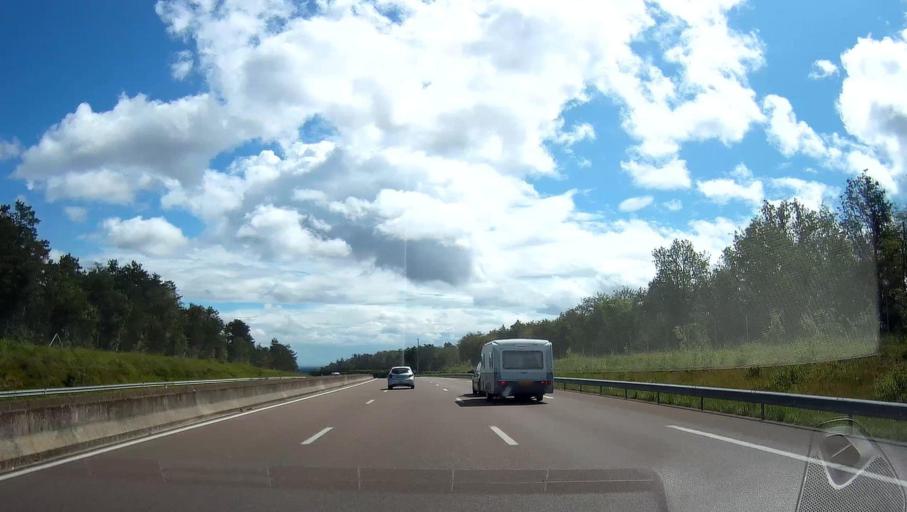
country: FR
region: Bourgogne
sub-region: Departement de la Cote-d'Or
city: Selongey
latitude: 47.6159
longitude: 5.1816
